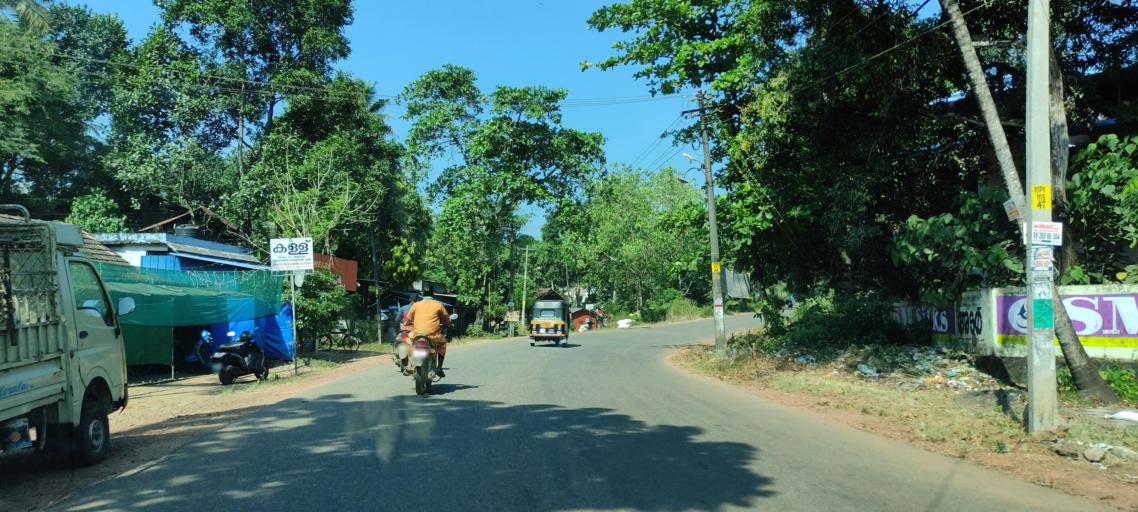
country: IN
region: Kerala
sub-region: Kollam
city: Panmana
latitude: 9.0487
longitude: 76.5673
